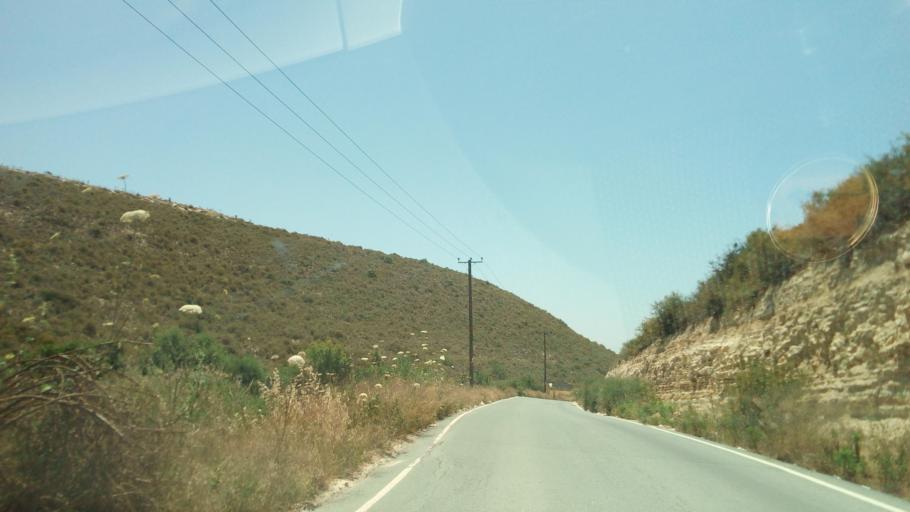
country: CY
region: Limassol
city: Ypsonas
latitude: 34.7362
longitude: 32.9476
